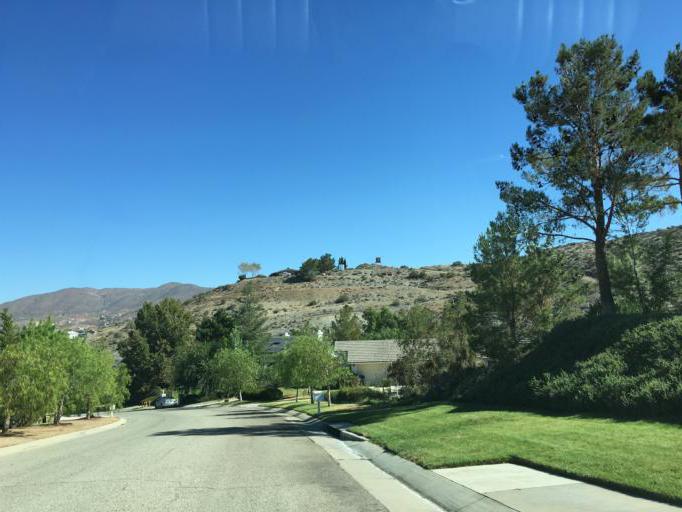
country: US
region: California
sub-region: Los Angeles County
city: Acton
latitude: 34.4698
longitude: -118.1547
